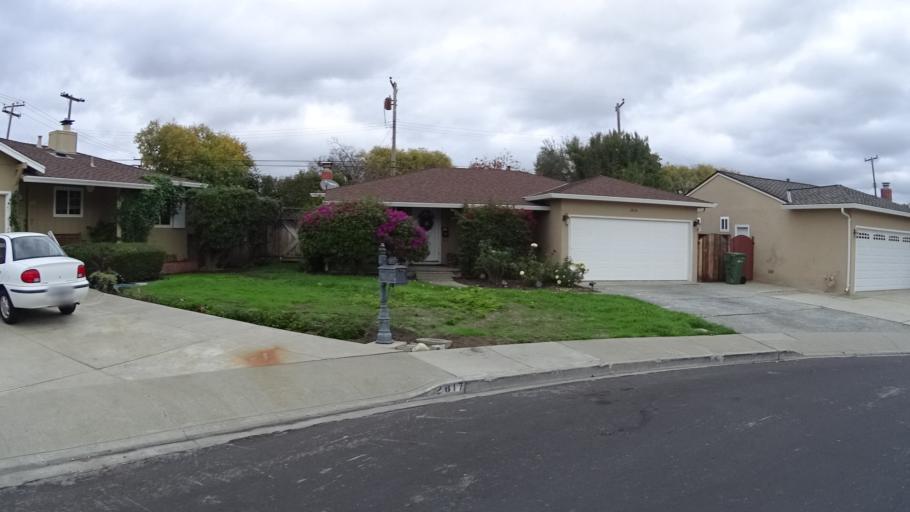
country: US
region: California
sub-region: Santa Clara County
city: Santa Clara
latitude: 37.3332
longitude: -121.9750
